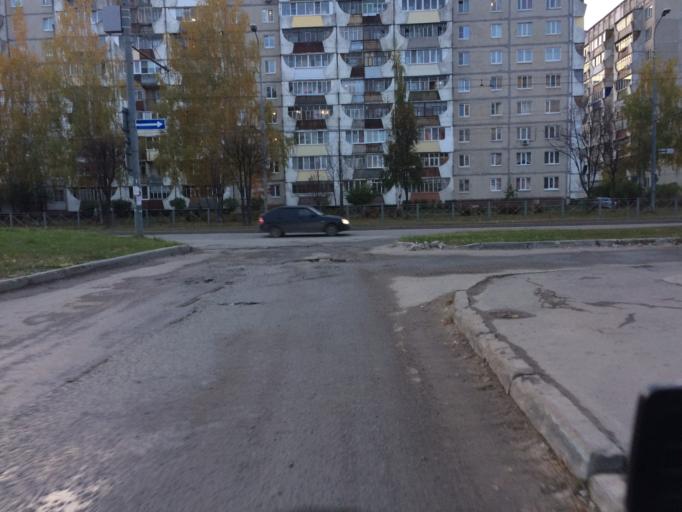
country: RU
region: Mariy-El
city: Yoshkar-Ola
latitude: 56.6324
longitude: 47.9198
